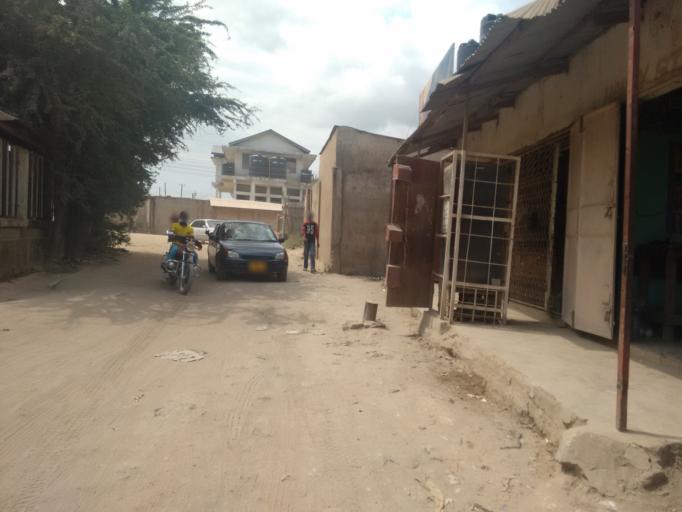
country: TZ
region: Dar es Salaam
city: Dar es Salaam
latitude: -6.8580
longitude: 39.2450
